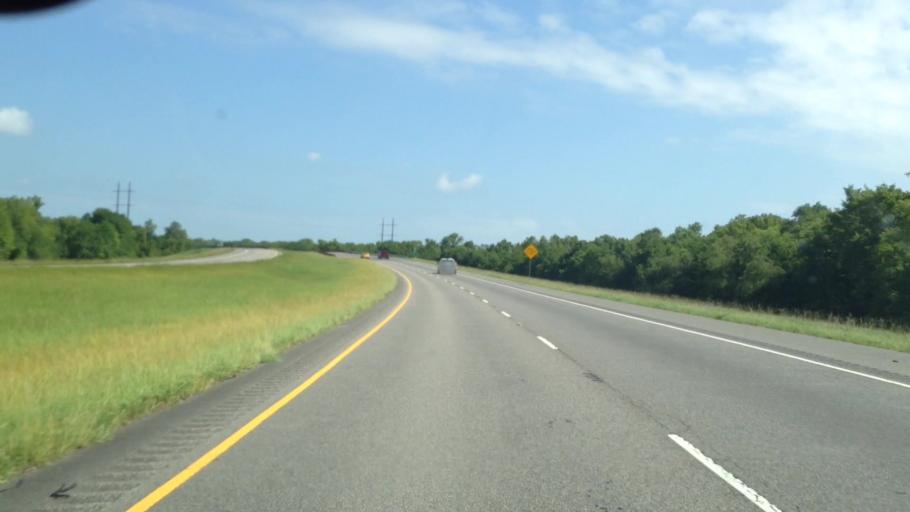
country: US
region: Louisiana
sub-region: Avoyelles Parish
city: Bunkie
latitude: 30.8951
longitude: -92.2269
